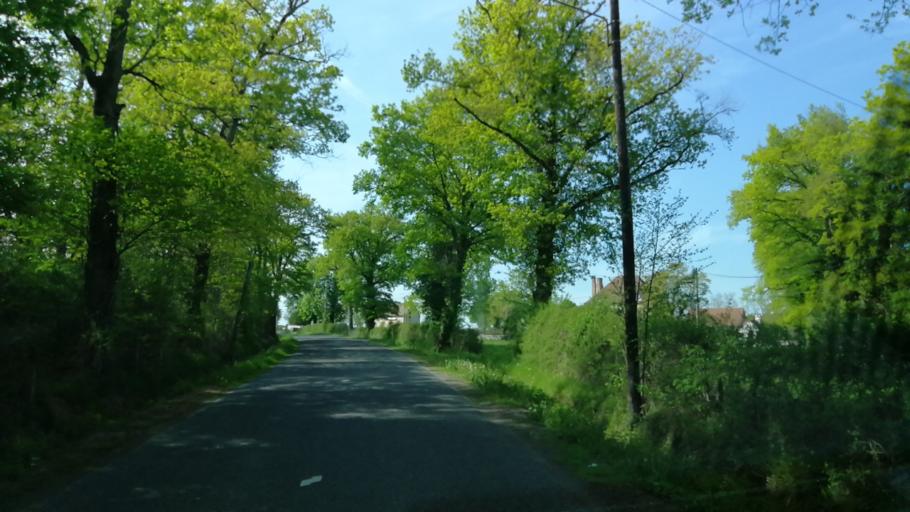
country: FR
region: Auvergne
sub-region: Departement de l'Allier
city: Neuilly-le-Real
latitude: 46.4908
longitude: 3.5185
